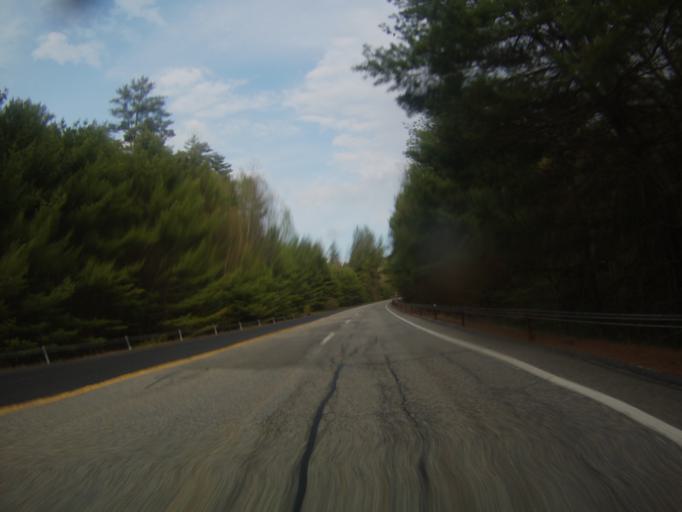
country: US
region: New York
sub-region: Essex County
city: Ticonderoga
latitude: 43.7438
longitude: -73.6298
